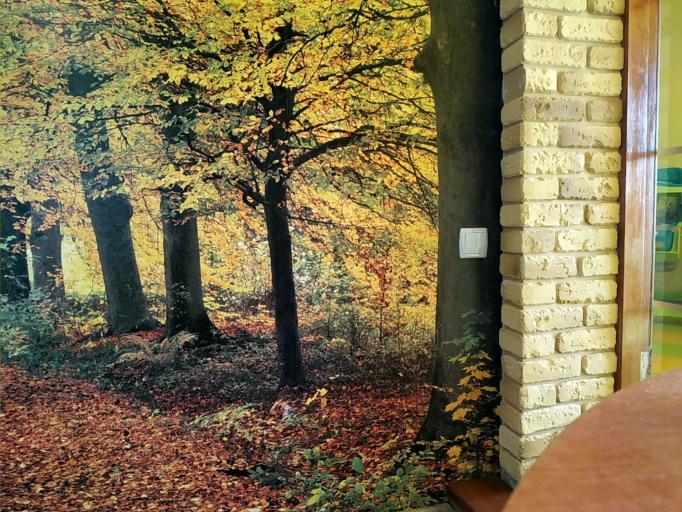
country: RU
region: Novgorod
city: Staraya Russa
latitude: 57.8326
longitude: 31.4849
